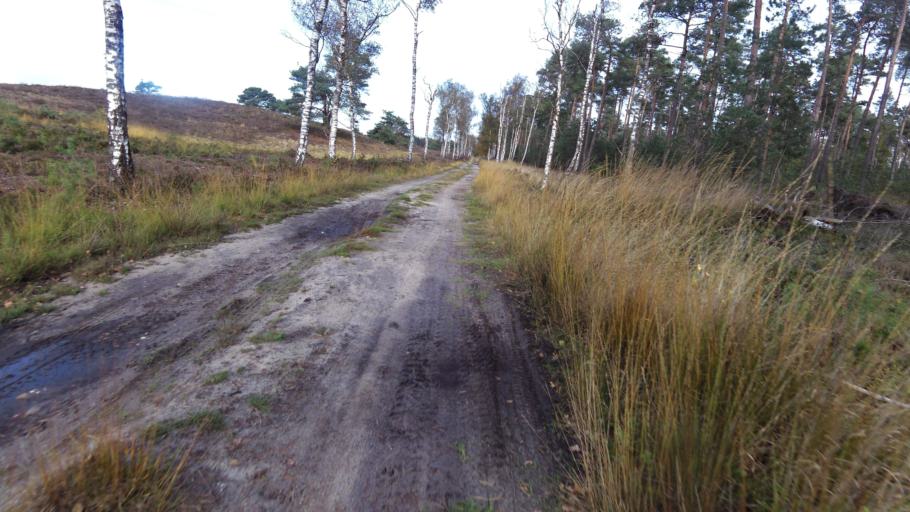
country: NL
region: Gelderland
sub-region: Gemeente Epe
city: Emst
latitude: 52.3384
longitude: 5.8943
